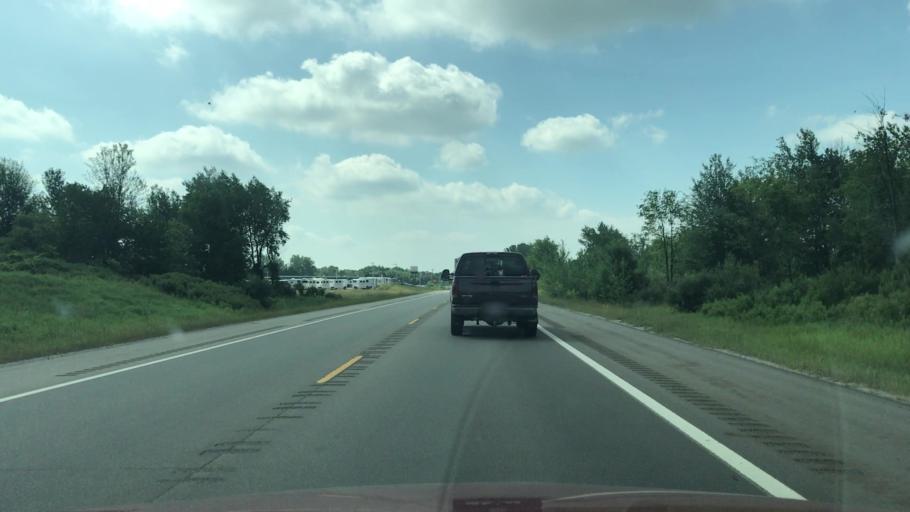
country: US
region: Michigan
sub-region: Kent County
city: Sparta
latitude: 43.1308
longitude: -85.7139
